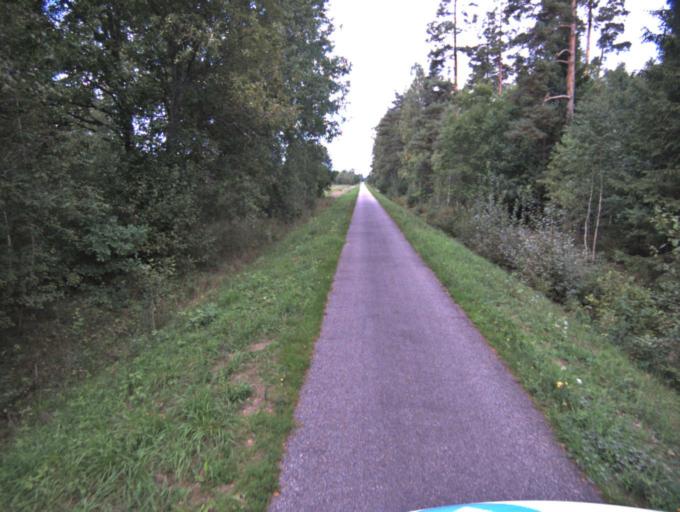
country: SE
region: Vaestra Goetaland
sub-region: Ulricehamns Kommun
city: Ulricehamn
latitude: 57.8317
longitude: 13.4190
